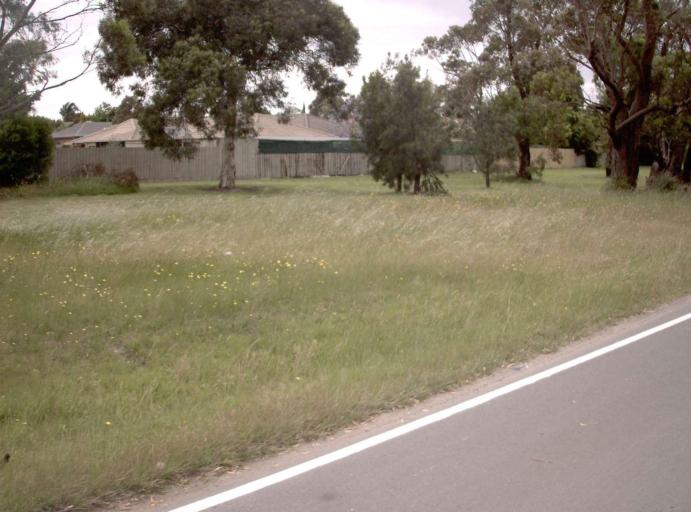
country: AU
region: Victoria
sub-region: Casey
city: Cranbourne North
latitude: -38.0690
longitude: 145.2682
